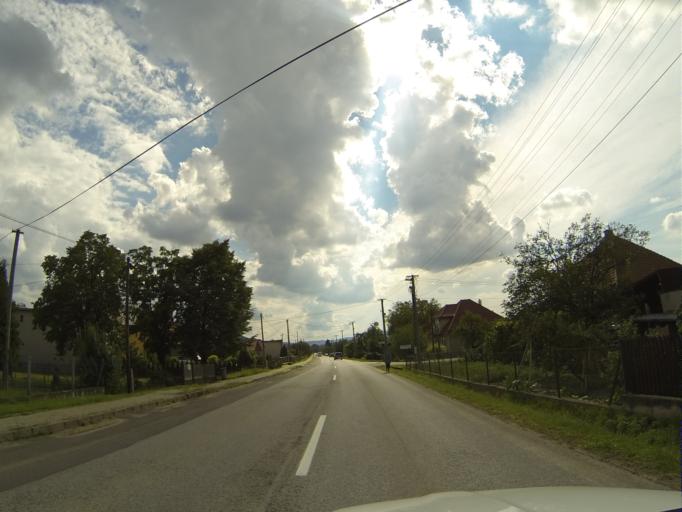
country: SK
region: Nitriansky
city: Novaky
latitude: 48.6483
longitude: 18.4939
